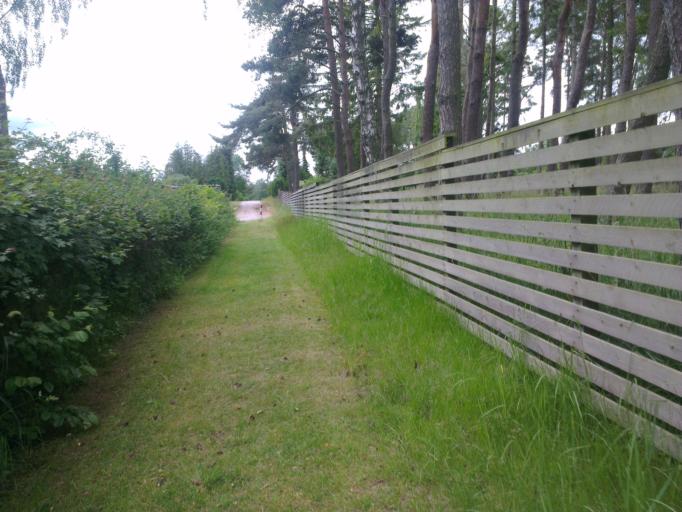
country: DK
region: Capital Region
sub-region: Frederikssund Kommune
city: Frederikssund
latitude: 55.8106
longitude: 12.0511
